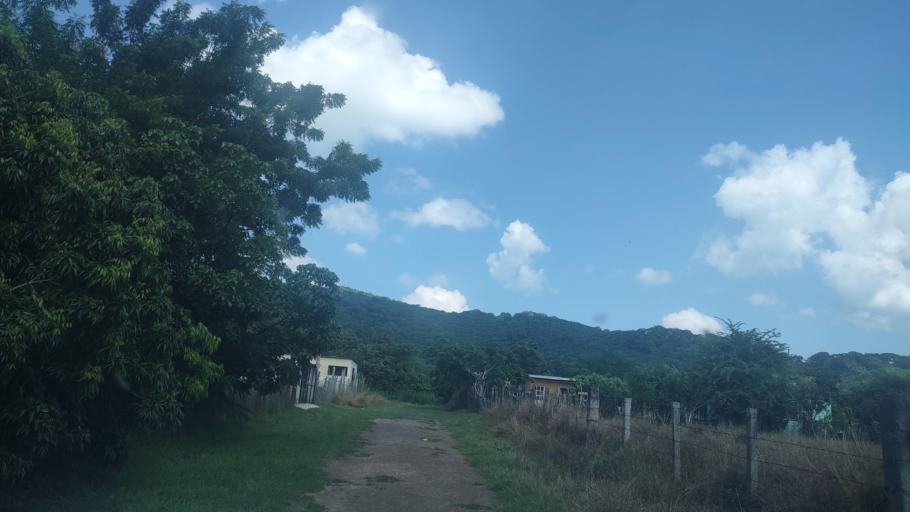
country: MX
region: Veracruz
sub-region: Chinampa de Gorostiza
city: Colonia las Flores
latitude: 21.3693
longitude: -97.6832
